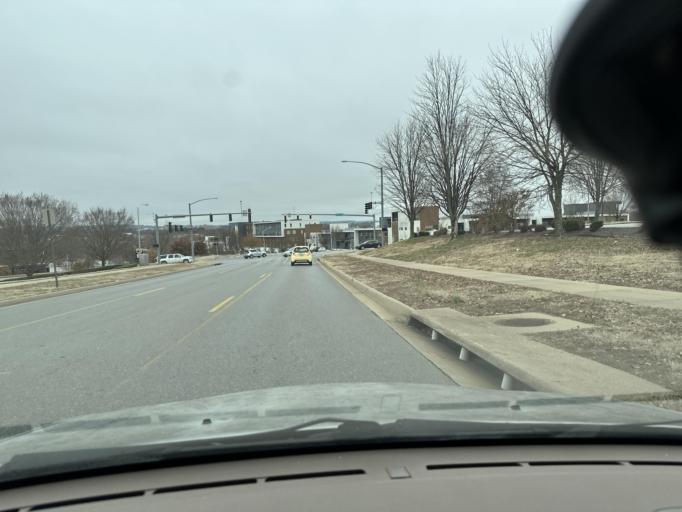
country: US
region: Arkansas
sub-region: Washington County
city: Johnson
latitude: 36.1255
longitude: -94.1560
